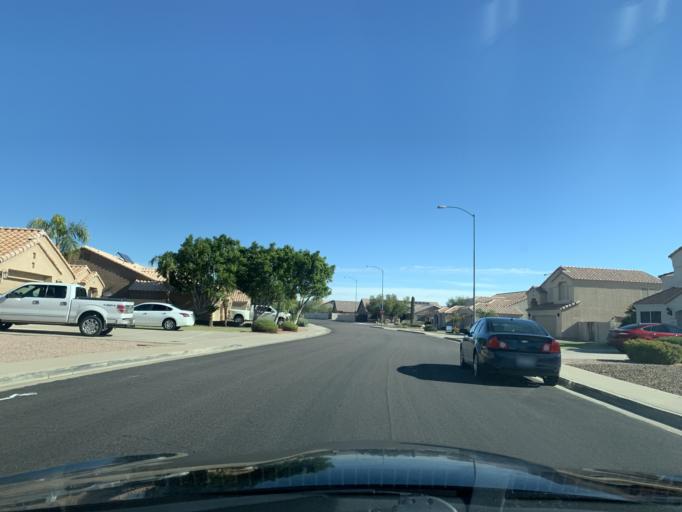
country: US
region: Arizona
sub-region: Pinal County
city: Apache Junction
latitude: 33.3834
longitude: -111.6253
